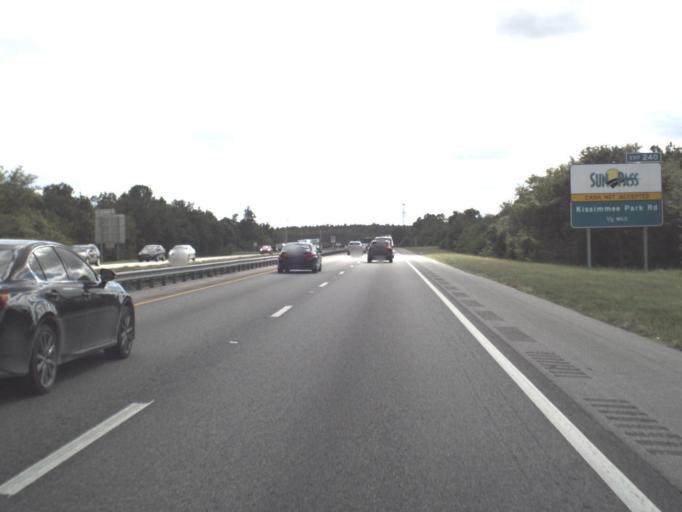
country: US
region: Florida
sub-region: Osceola County
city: Saint Cloud
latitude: 28.2309
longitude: -81.3234
